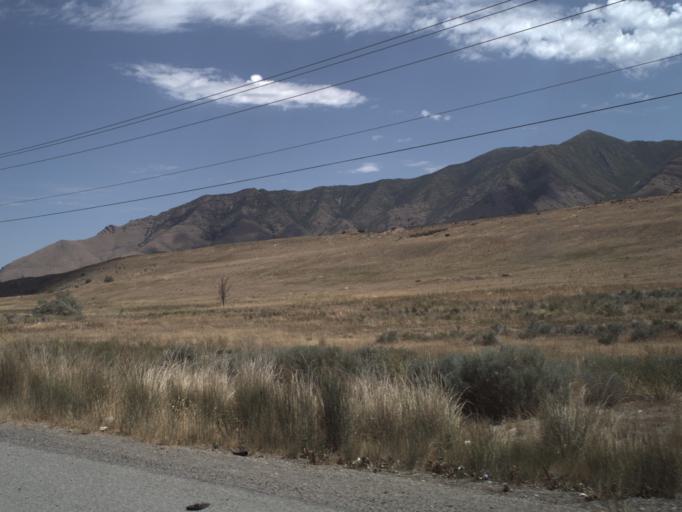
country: US
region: Utah
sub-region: Tooele County
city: Stansbury park
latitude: 40.6392
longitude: -112.2884
